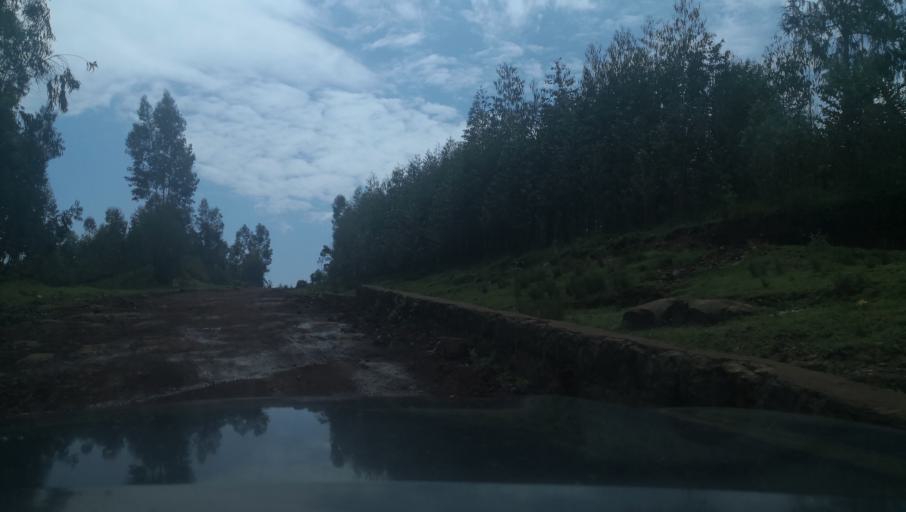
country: ET
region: Southern Nations, Nationalities, and People's Region
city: Butajira
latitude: 8.3039
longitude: 38.4570
